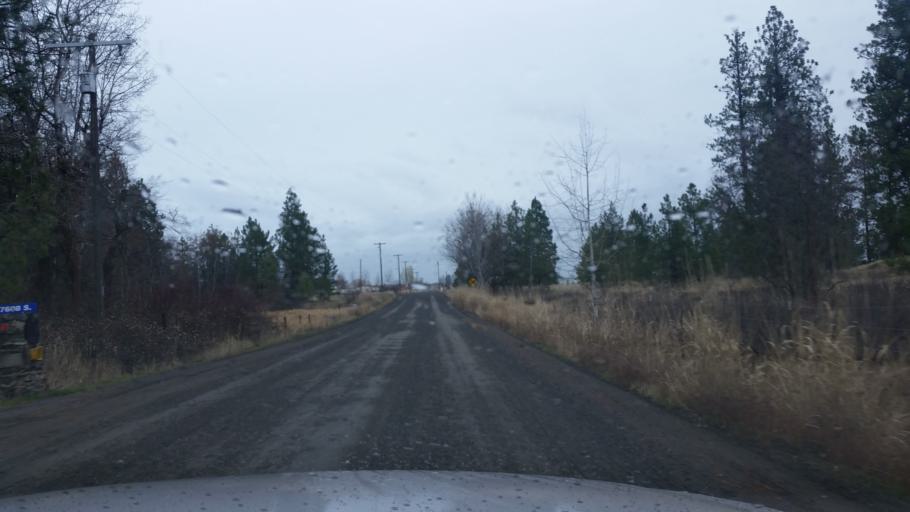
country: US
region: Washington
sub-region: Spokane County
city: Fairchild Air Force Base
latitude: 47.5836
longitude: -117.6289
